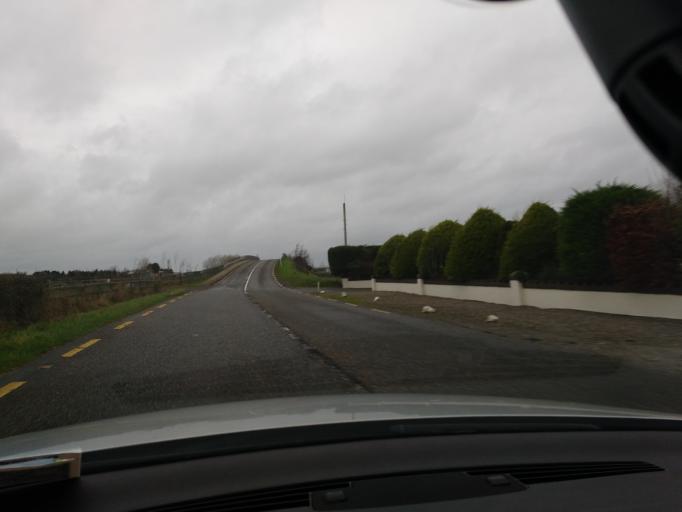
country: IE
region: Munster
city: Thurles
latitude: 52.6708
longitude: -7.6905
